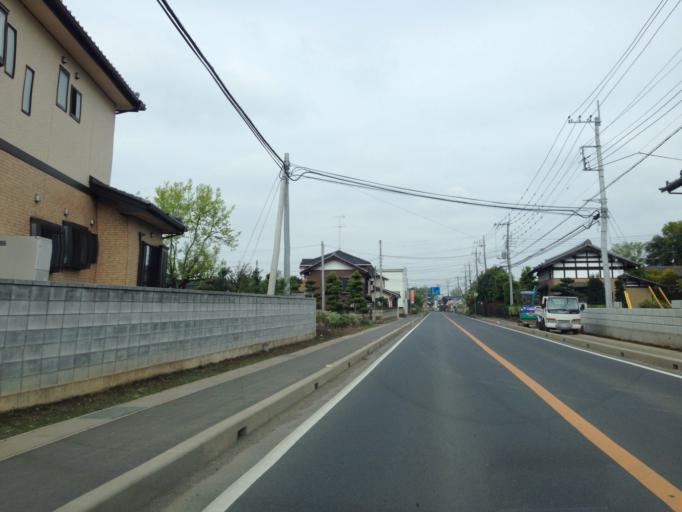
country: JP
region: Ibaraki
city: Ishige
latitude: 36.1580
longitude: 139.9372
